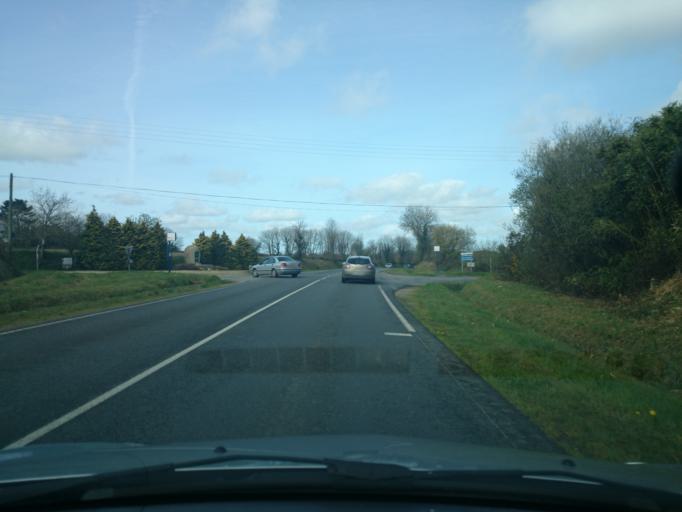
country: FR
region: Brittany
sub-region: Departement du Finistere
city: Gouesnou
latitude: 48.4414
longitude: -4.4510
